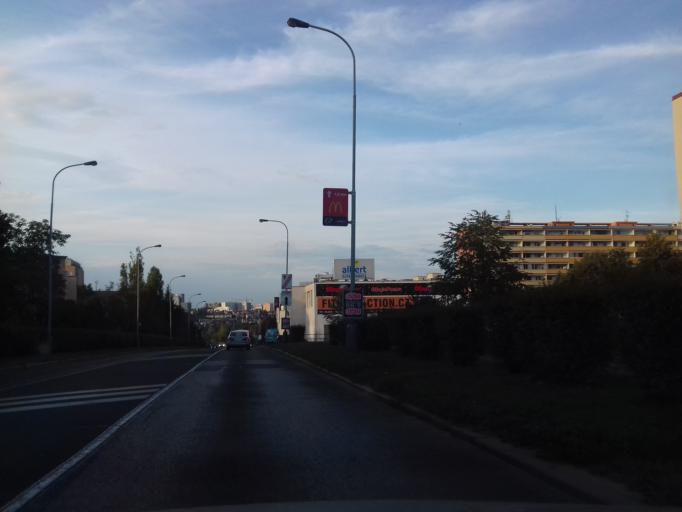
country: CZ
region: Praha
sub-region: Praha 4
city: Hodkovicky
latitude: 50.0251
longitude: 14.4515
